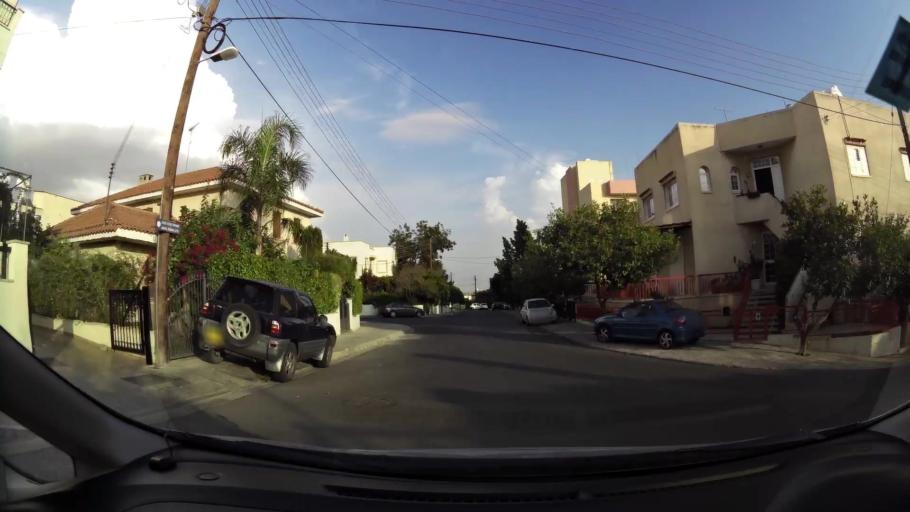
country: CY
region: Lefkosia
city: Nicosia
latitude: 35.1617
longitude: 33.3902
